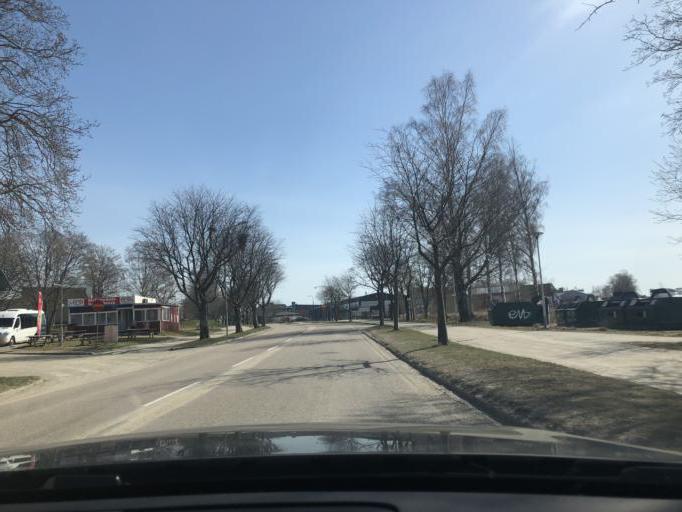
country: SE
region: Gaevleborg
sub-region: Hudiksvalls Kommun
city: Hudiksvall
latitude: 61.7265
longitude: 17.1227
